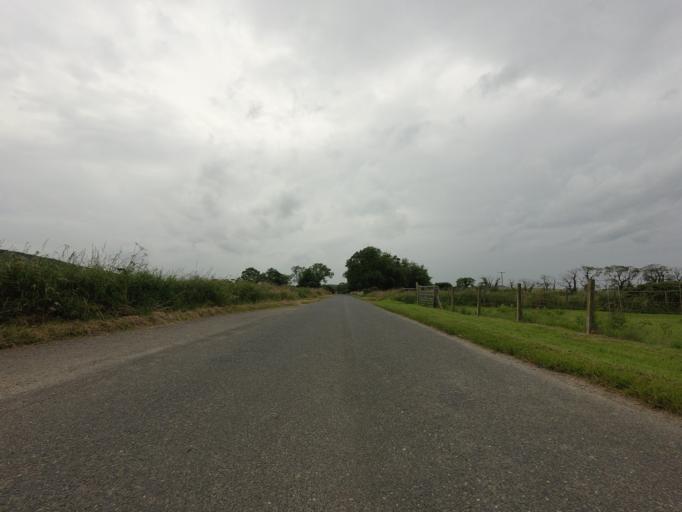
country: GB
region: Scotland
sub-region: Aberdeenshire
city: Portsoy
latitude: 57.6624
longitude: -2.7388
